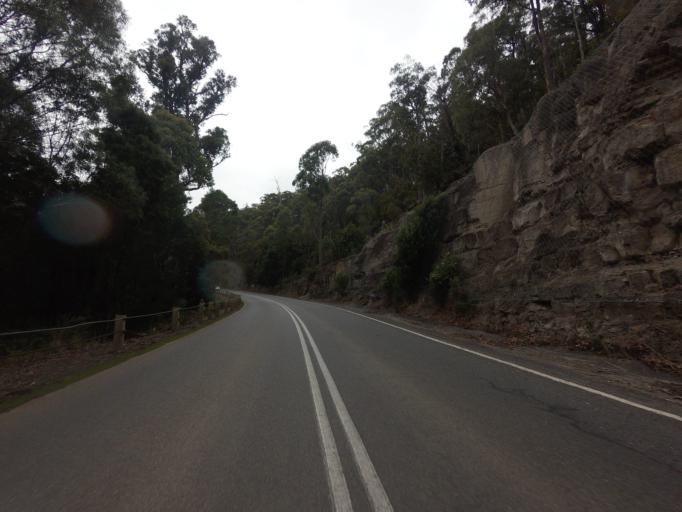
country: AU
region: Tasmania
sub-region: Derwent Valley
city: New Norfolk
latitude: -42.6852
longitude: 146.7270
